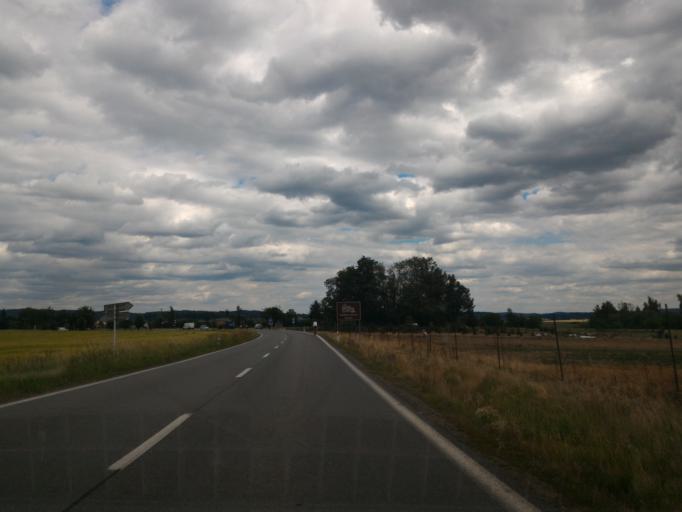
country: CZ
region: Vysocina
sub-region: Okres Jihlava
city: Telc
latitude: 49.1843
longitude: 15.4352
